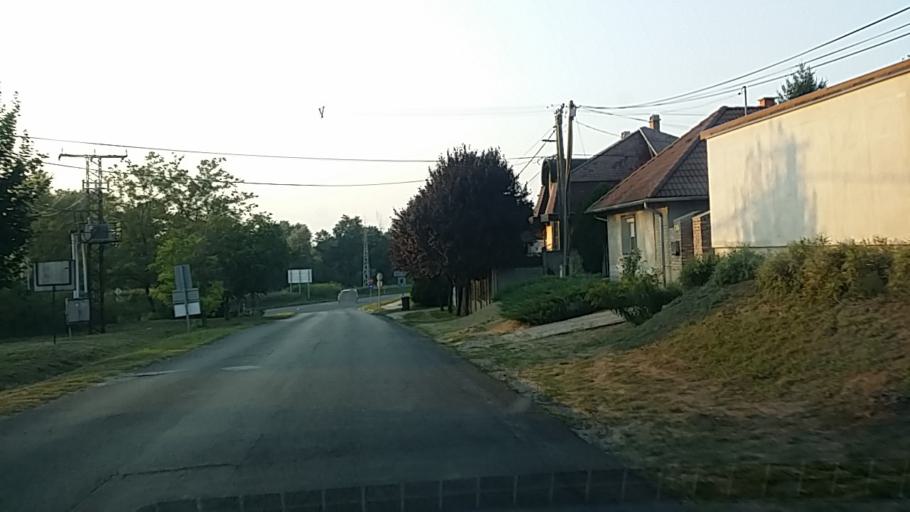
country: HU
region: Tolna
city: Dunafoldvar
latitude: 46.8271
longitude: 18.9078
